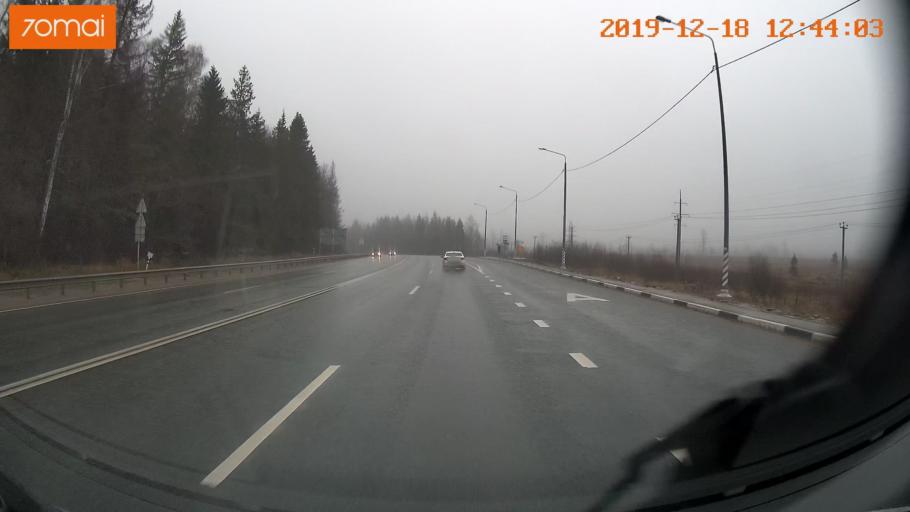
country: RU
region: Moskovskaya
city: Vysokovsk
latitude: 56.2152
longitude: 36.6453
